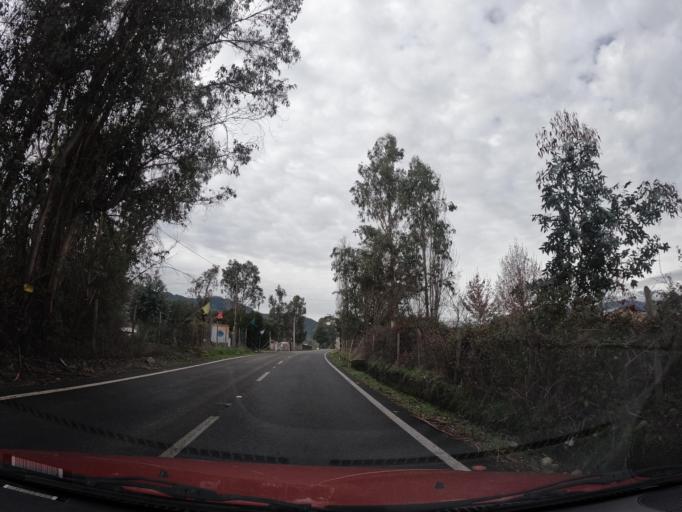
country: CL
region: Maule
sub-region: Provincia de Linares
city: Linares
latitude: -35.9252
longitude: -71.4183
